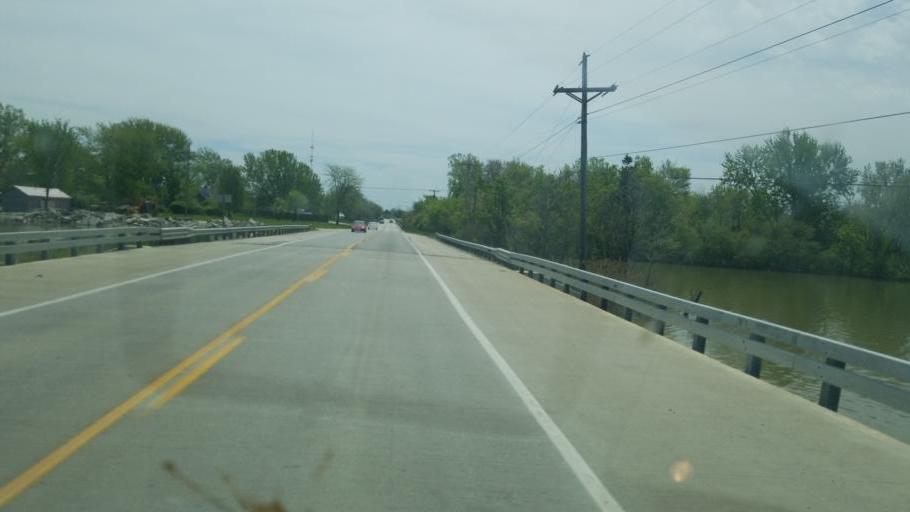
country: US
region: Ohio
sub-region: Ottawa County
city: Oak Harbor
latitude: 41.5850
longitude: -83.0953
